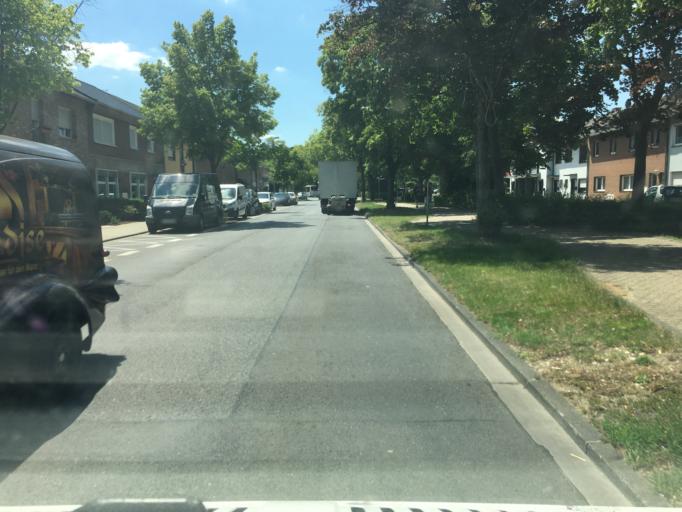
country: DE
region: North Rhine-Westphalia
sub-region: Regierungsbezirk Koln
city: Frechen
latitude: 50.8752
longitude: 6.8153
